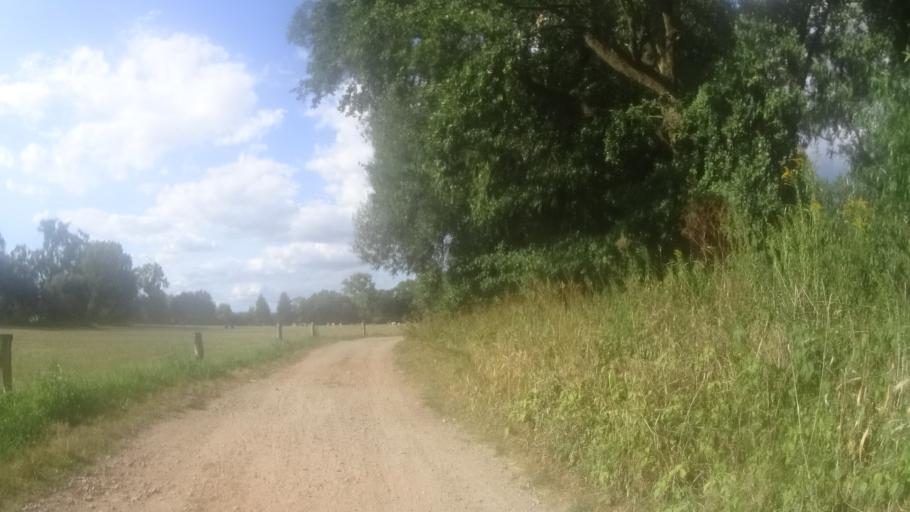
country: CZ
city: Albrechtice nad Orlici
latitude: 50.1586
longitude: 16.0408
